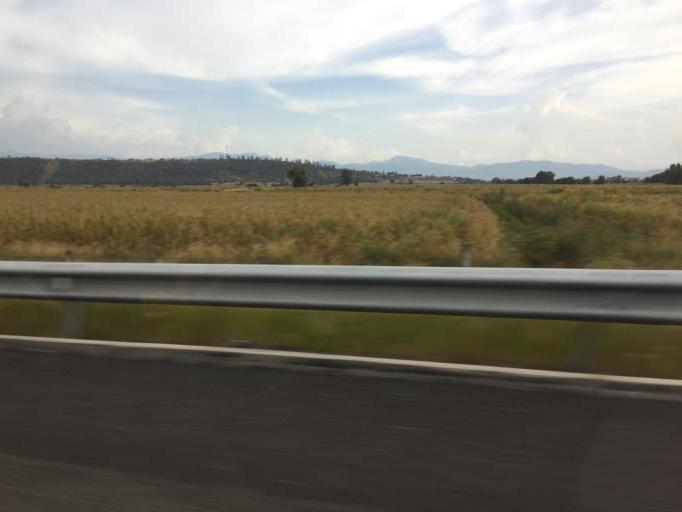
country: MX
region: Michoacan
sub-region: Alvaro Obregon
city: Tzintzimeo
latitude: 19.8906
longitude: -100.9746
